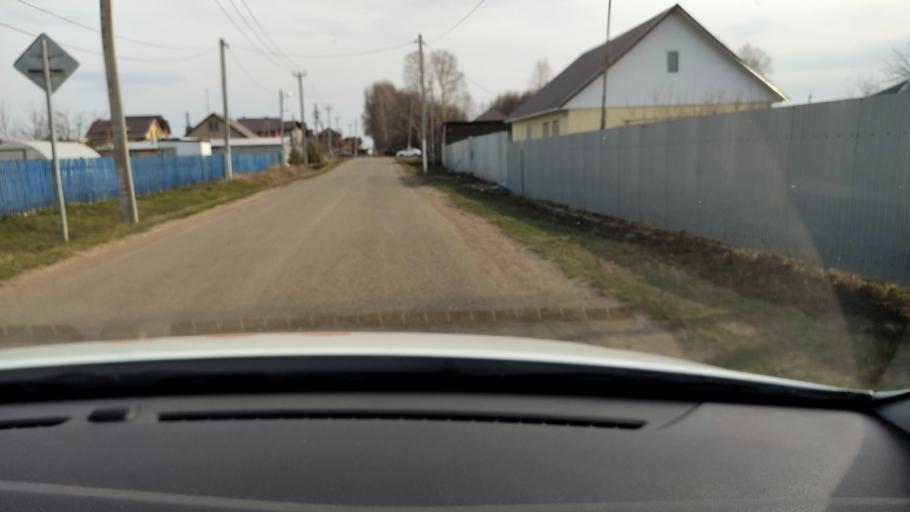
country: RU
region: Tatarstan
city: Stolbishchi
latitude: 55.6457
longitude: 49.3114
